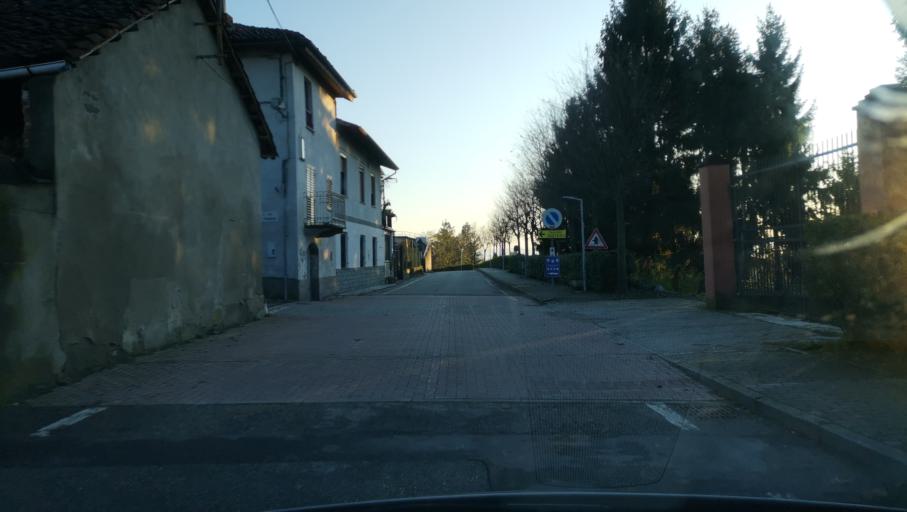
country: IT
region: Piedmont
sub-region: Provincia di Torino
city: Cinzano
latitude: 45.0929
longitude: 7.9239
